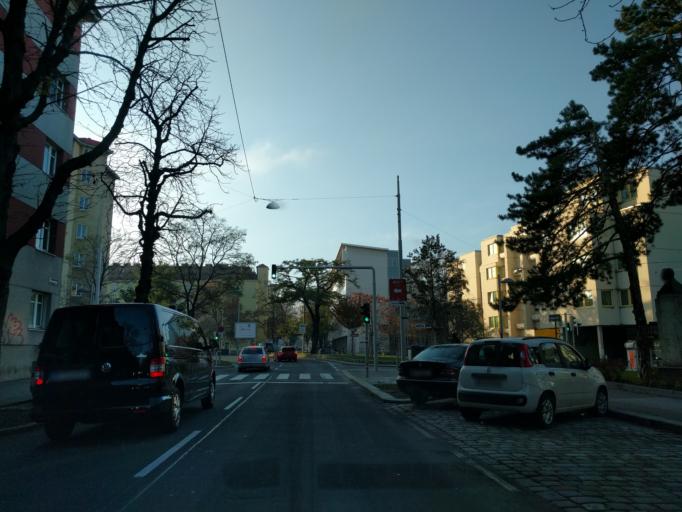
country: AT
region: Vienna
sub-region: Wien Stadt
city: Vienna
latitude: 48.2094
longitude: 16.3157
